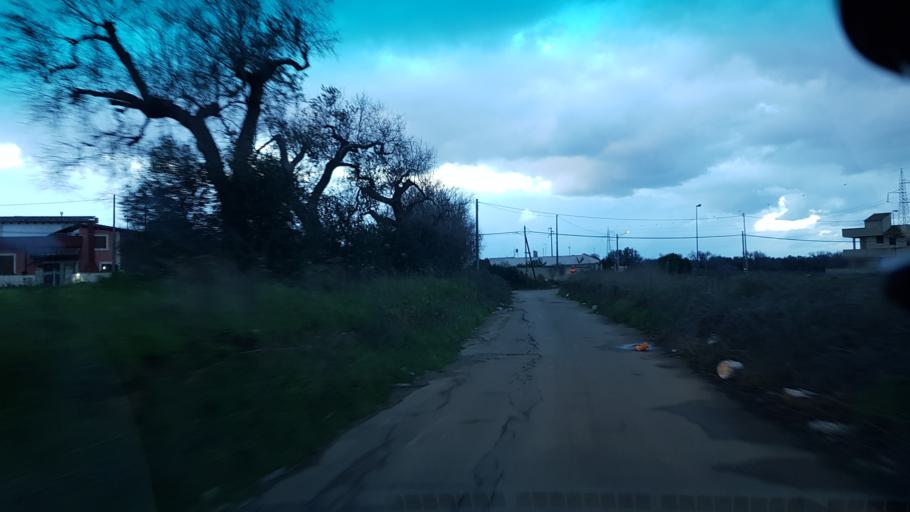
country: IT
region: Apulia
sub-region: Provincia di Brindisi
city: Torchiarolo
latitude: 40.4901
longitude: 18.0540
